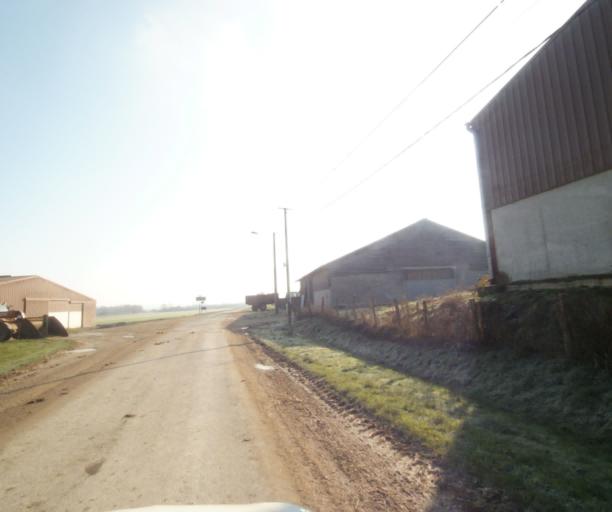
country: FR
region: Champagne-Ardenne
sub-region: Departement de la Haute-Marne
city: Montier-en-Der
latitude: 48.4955
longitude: 4.7257
